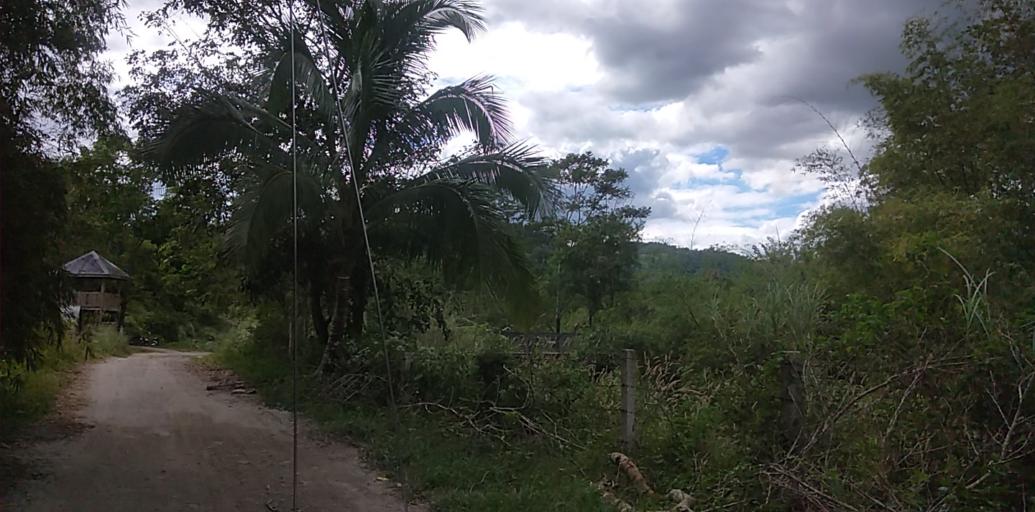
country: PH
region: Central Luzon
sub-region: Province of Pampanga
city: Babo-Pangulo
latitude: 15.1113
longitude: 120.5012
